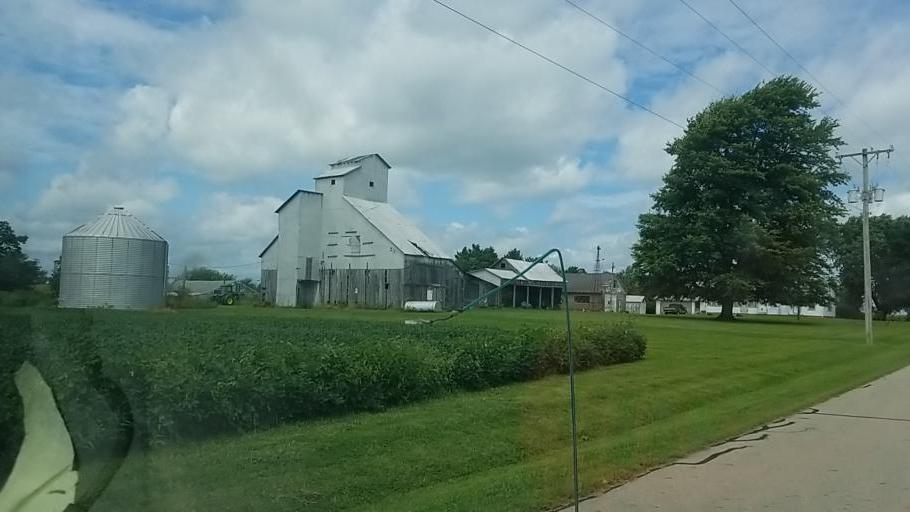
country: US
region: Ohio
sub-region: Fayette County
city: Jeffersonville
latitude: 39.6763
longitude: -83.5752
